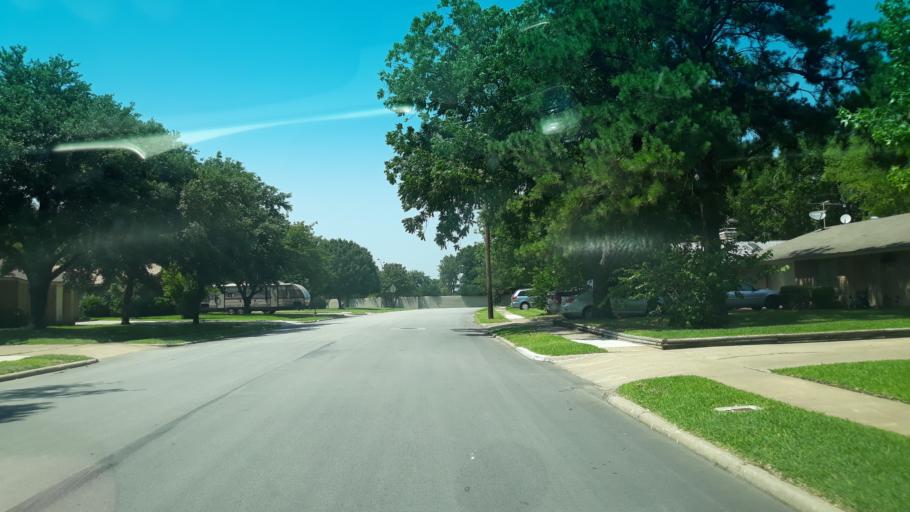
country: US
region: Texas
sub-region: Dallas County
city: Irving
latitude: 32.8547
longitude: -96.9677
